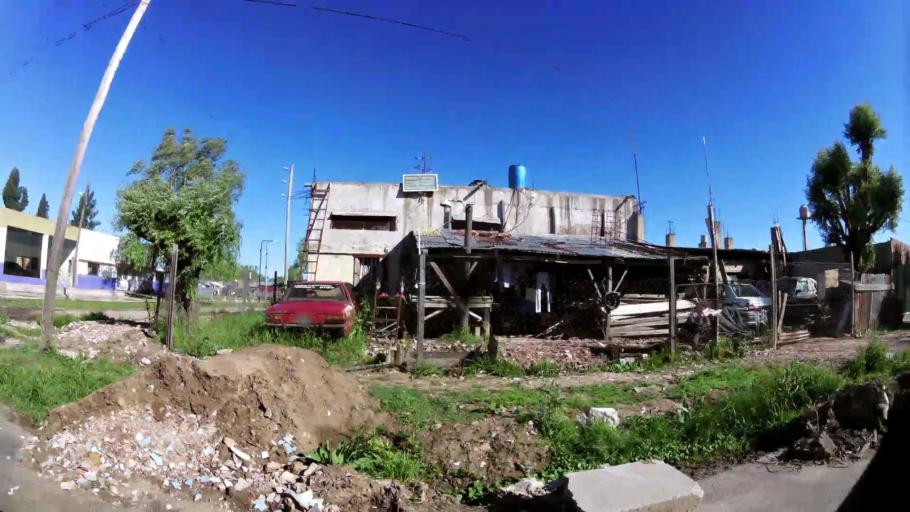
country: AR
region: Buenos Aires
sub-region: Partido de Quilmes
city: Quilmes
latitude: -34.7586
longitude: -58.3179
